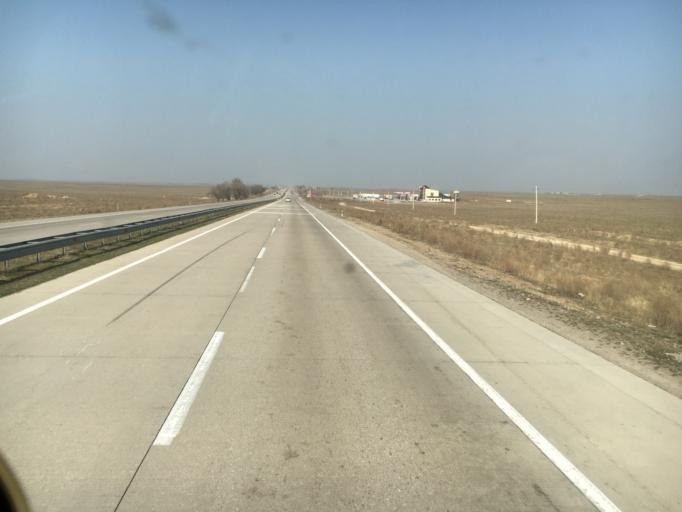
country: KZ
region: Ongtustik Qazaqstan
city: Temirlanovka
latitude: 42.8380
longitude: 69.1119
